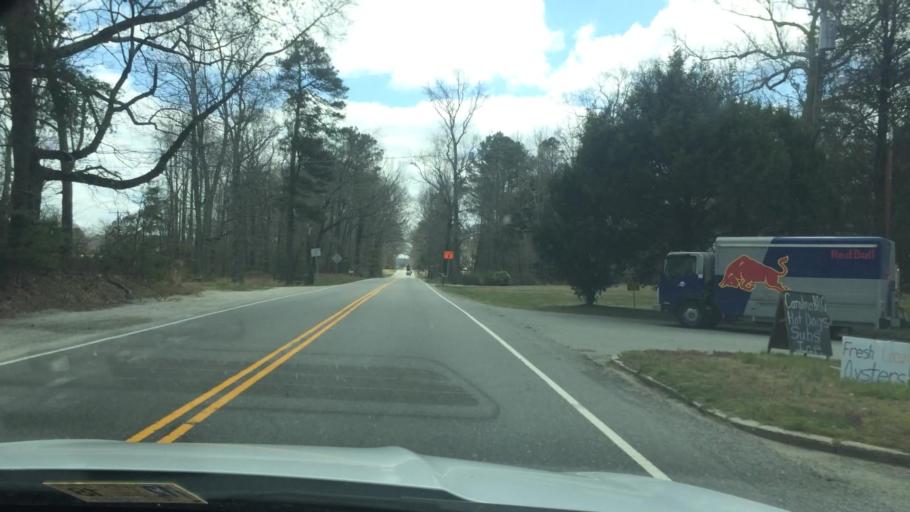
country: US
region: Virginia
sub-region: King William County
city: West Point
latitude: 37.4355
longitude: -76.8350
